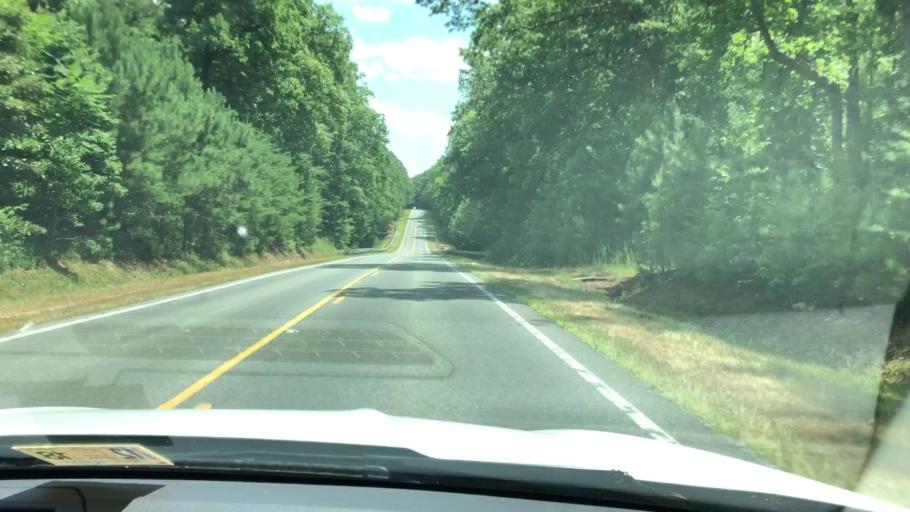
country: US
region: Virginia
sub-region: Lancaster County
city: Lancaster
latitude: 37.8183
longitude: -76.5516
